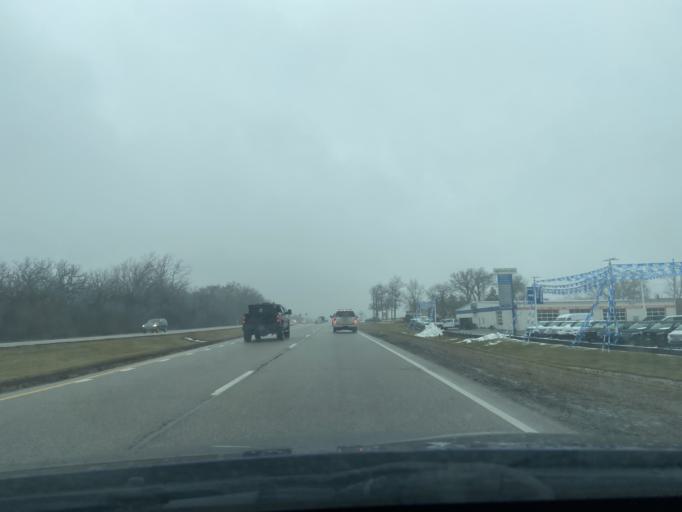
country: US
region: Illinois
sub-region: Lake County
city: Wauconda
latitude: 42.2821
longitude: -88.1555
